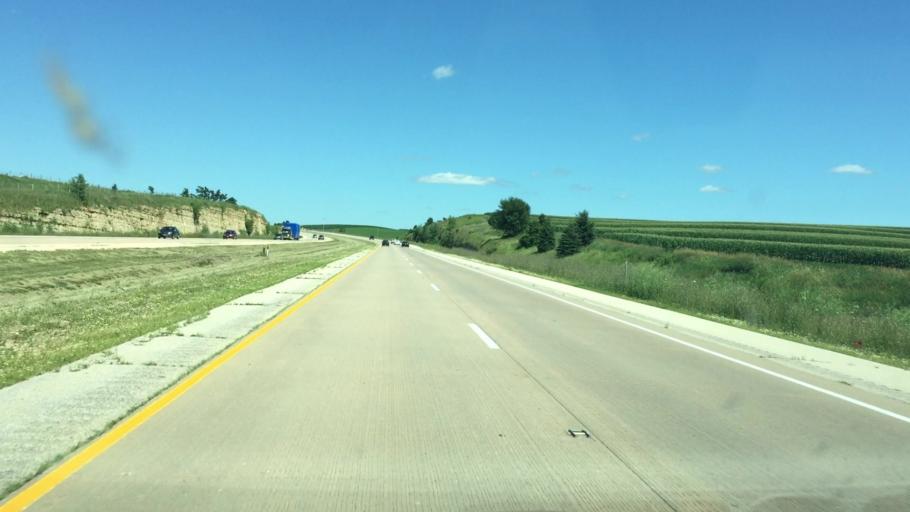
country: US
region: Wisconsin
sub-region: Grant County
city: Platteville
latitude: 42.7373
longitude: -90.4165
